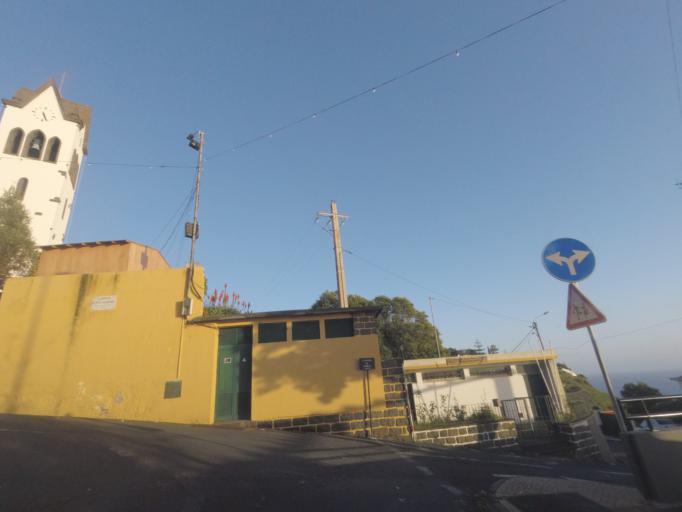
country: PT
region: Madeira
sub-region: Funchal
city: Funchal
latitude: 32.6493
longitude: -16.8828
